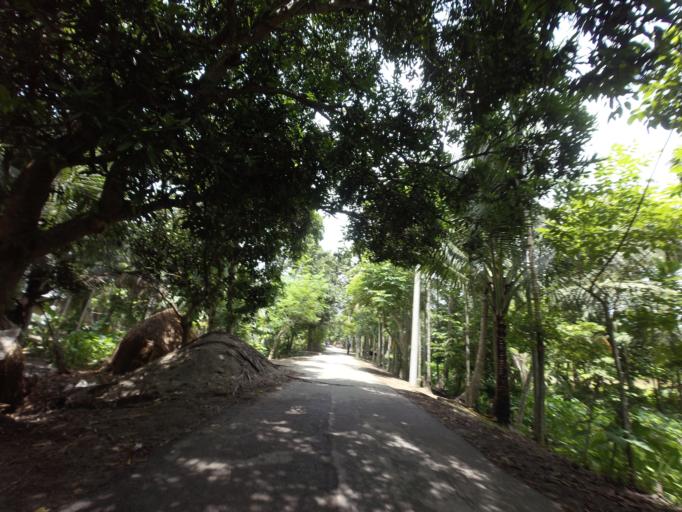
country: BD
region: Khulna
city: Kalia
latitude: 23.0438
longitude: 89.6540
